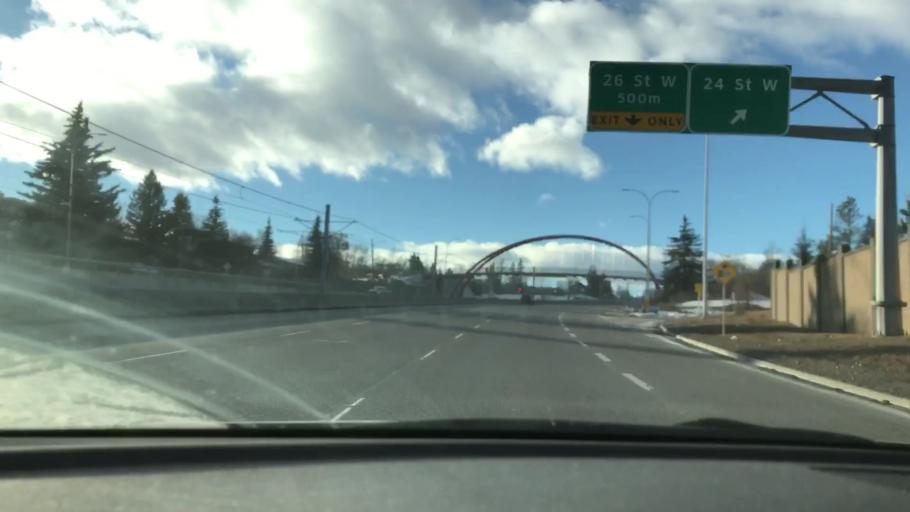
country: CA
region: Alberta
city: Calgary
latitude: 51.0422
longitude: -114.1163
